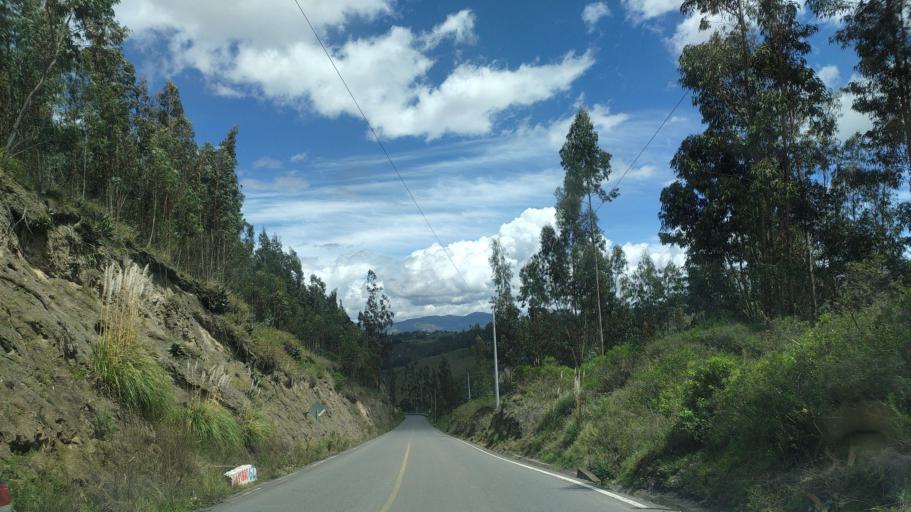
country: EC
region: Chimborazo
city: Riobamba
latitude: -1.6603
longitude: -78.5823
